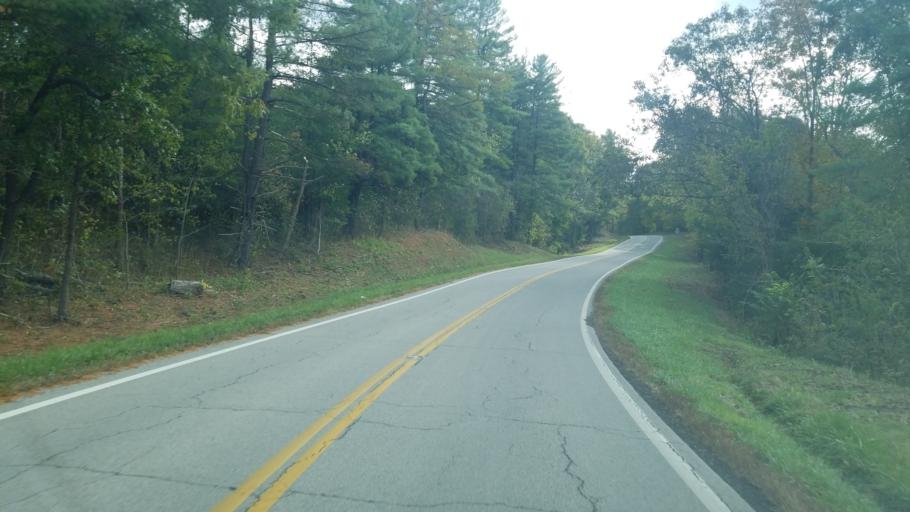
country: US
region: Ohio
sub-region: Vinton County
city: McArthur
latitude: 39.1625
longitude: -82.4392
